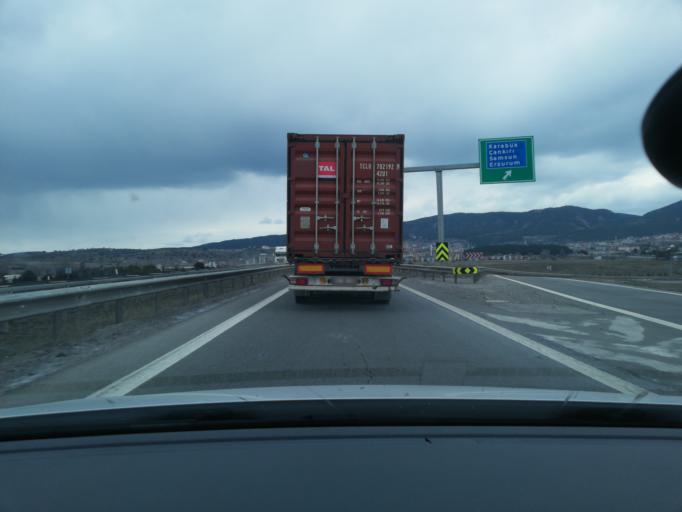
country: TR
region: Bolu
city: Gerede
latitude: 40.7777
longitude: 32.2113
